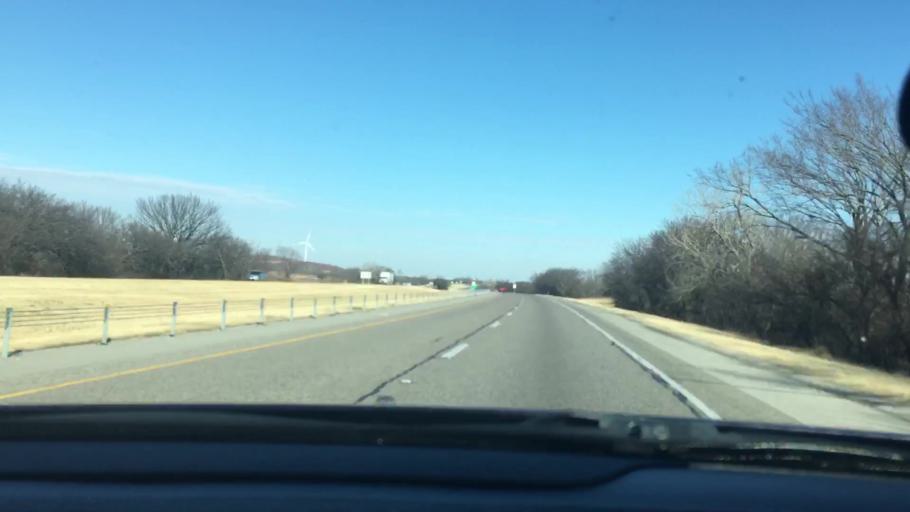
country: US
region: Oklahoma
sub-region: Murray County
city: Davis
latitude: 34.3855
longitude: -97.1417
